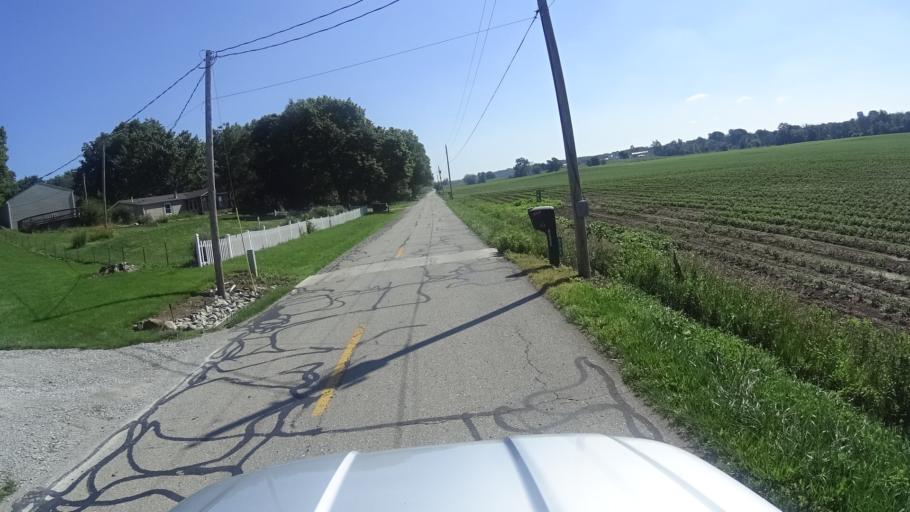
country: US
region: Indiana
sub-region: Madison County
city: Ingalls
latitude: 39.9830
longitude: -85.7814
